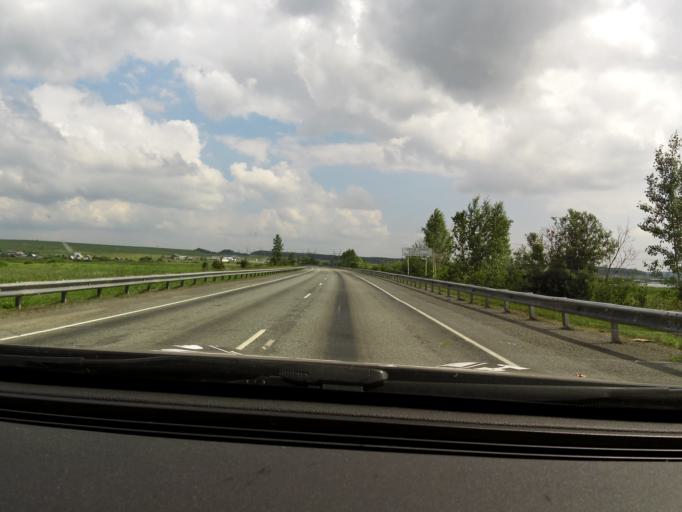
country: RU
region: Sverdlovsk
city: Achit
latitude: 56.7848
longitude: 57.8928
